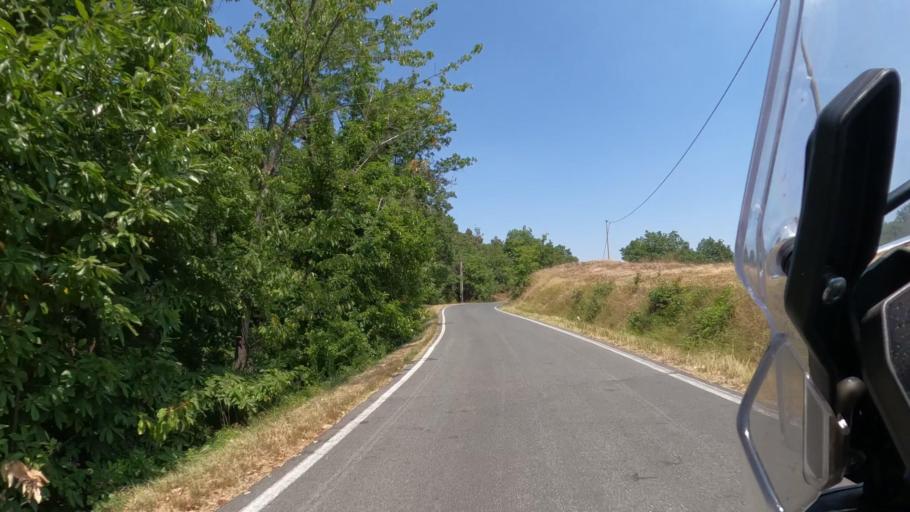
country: IT
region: Piedmont
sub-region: Provincia di Alessandria
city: Morbello
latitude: 44.5603
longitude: 8.5143
